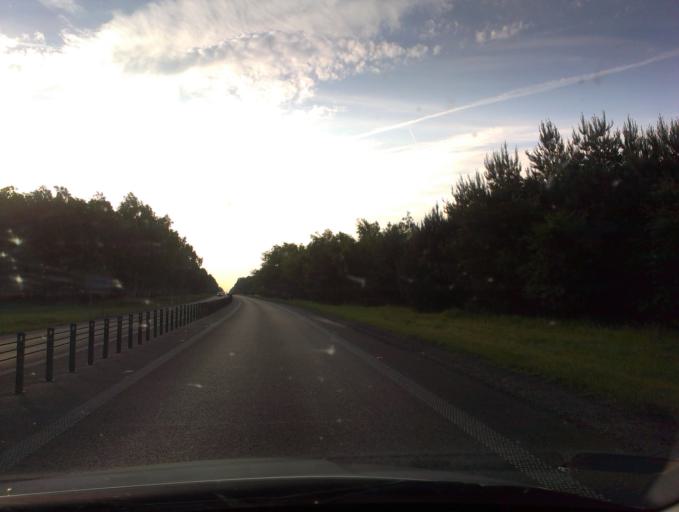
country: PL
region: Greater Poland Voivodeship
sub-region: Powiat leszczynski
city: Rydzyna
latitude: 51.8003
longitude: 16.6494
